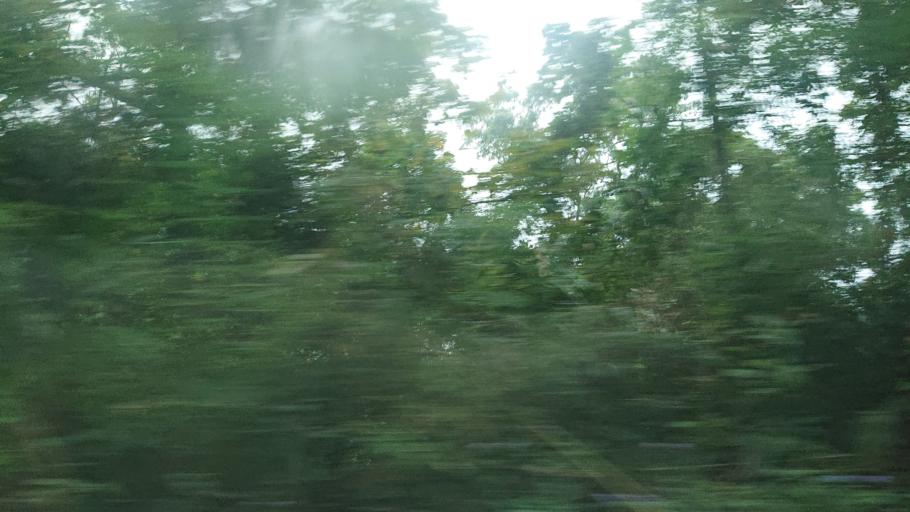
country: TW
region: Taiwan
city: Lugu
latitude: 23.5947
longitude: 120.7147
